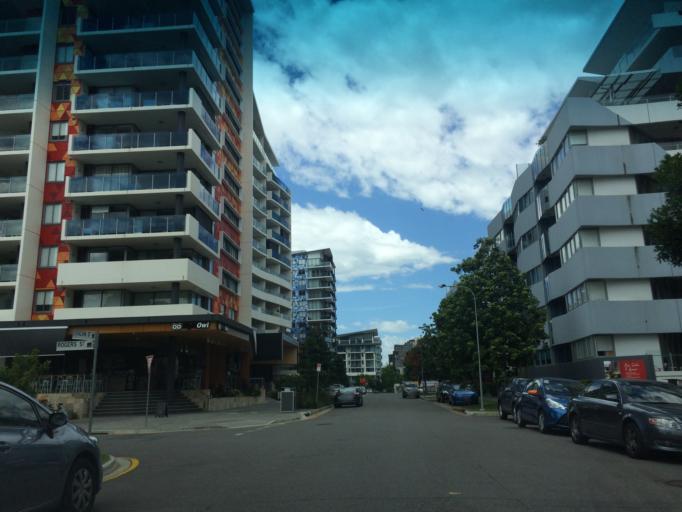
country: AU
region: Queensland
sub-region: Brisbane
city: Toowong
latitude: -27.4838
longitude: 153.0002
